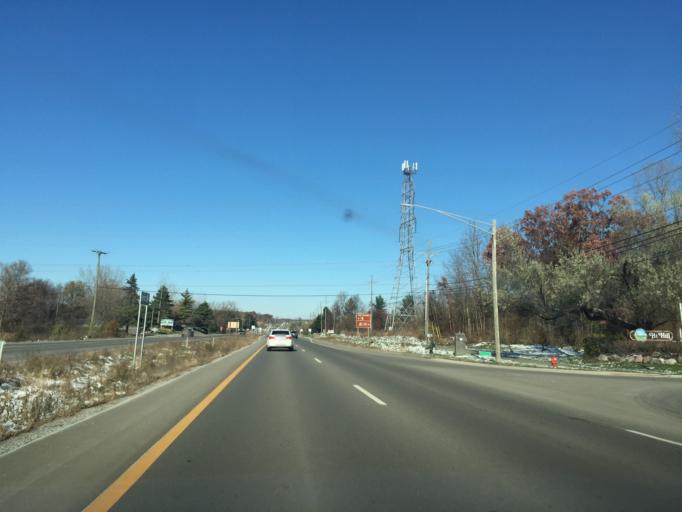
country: US
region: Michigan
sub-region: Oakland County
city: Auburn Hills
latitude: 42.7313
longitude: -83.2440
